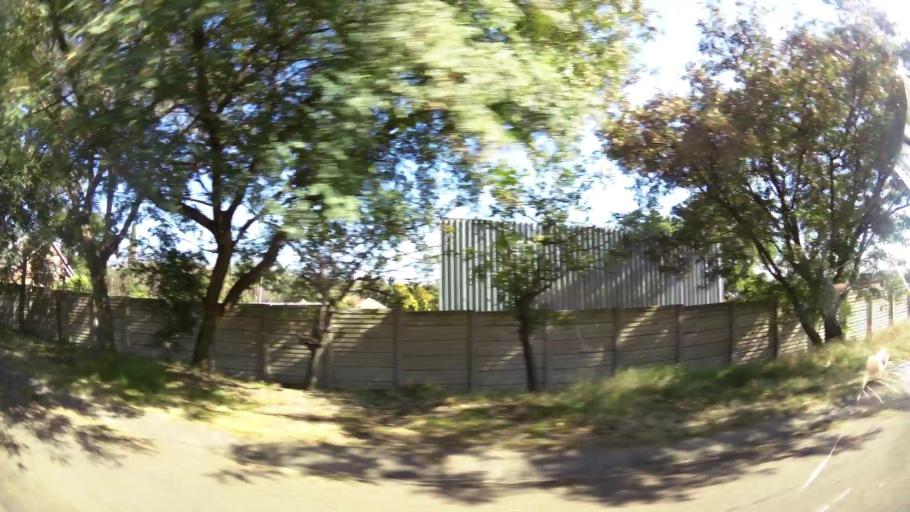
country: ZA
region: Mpumalanga
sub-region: Nkangala District Municipality
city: Witbank
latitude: -25.8652
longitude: 29.2426
